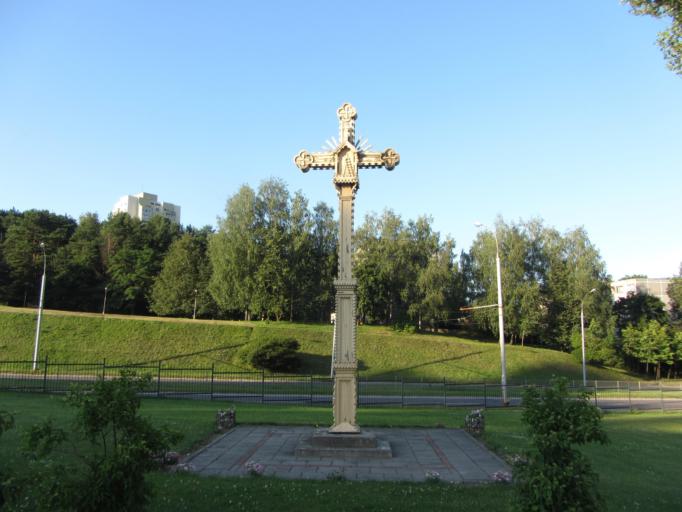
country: LT
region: Vilnius County
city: Lazdynai
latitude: 54.6793
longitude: 25.2117
